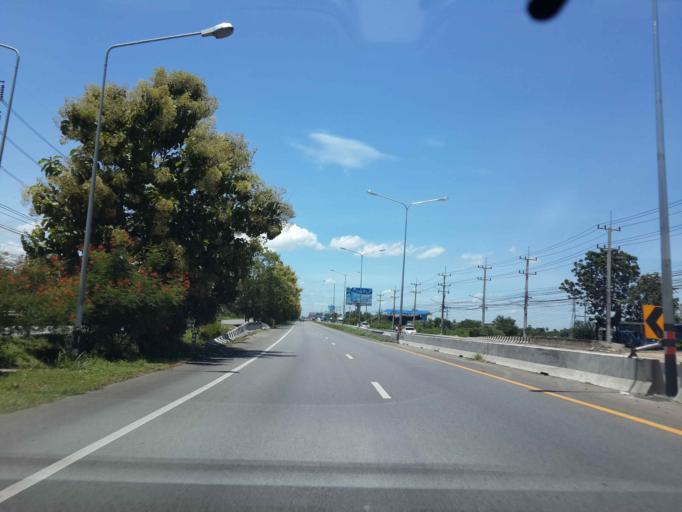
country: TH
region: Phetchaburi
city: Khao Yoi
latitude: 13.2514
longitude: 99.8256
